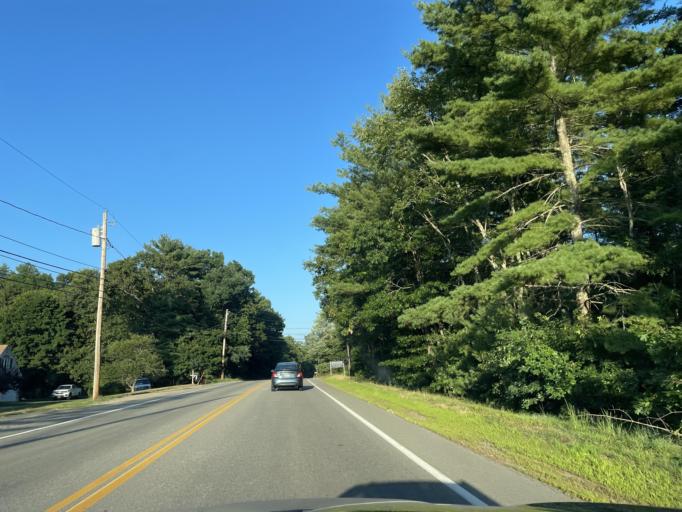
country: US
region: Massachusetts
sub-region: Plymouth County
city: Halifax
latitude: 41.9958
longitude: -70.8864
